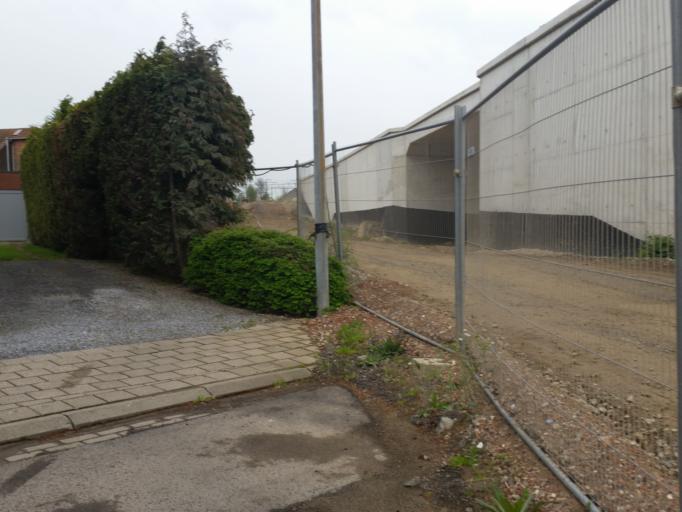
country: BE
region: Flanders
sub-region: Provincie Antwerpen
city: Mechelen
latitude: 51.0094
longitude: 4.4763
